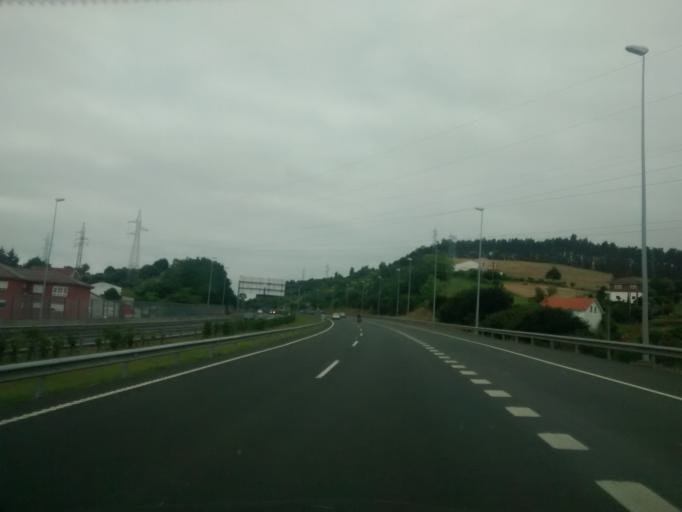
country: ES
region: Cantabria
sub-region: Provincia de Cantabria
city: Reocin
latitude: 43.3538
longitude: -4.0904
